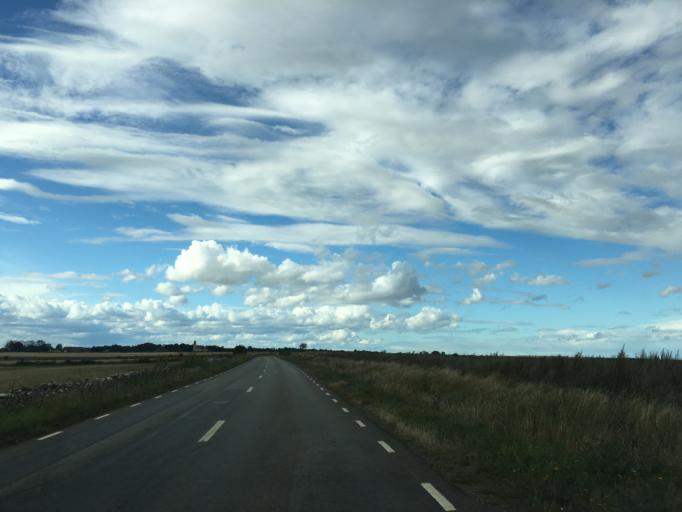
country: SE
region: Kalmar
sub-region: Morbylanga Kommun
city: Moerbylanga
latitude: 56.3936
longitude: 16.4370
